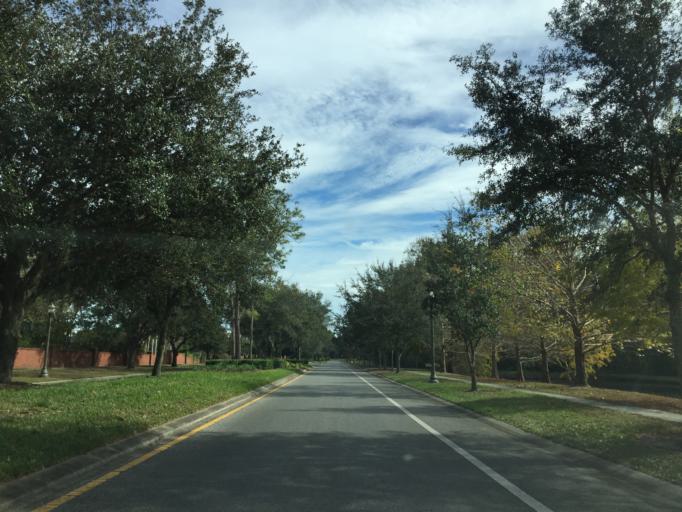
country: US
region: Florida
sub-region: Seminole County
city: Oviedo
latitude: 28.6770
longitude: -81.2435
